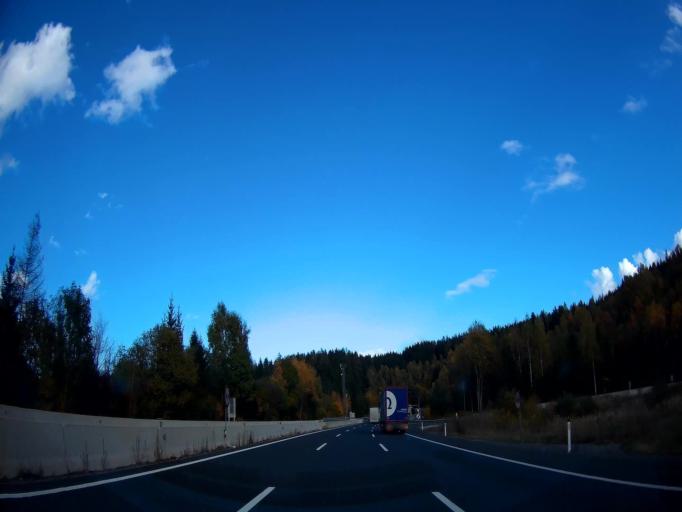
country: AT
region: Carinthia
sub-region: Politischer Bezirk Wolfsberg
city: Bad Sankt Leonhard im Lavanttal
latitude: 46.9349
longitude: 14.8528
